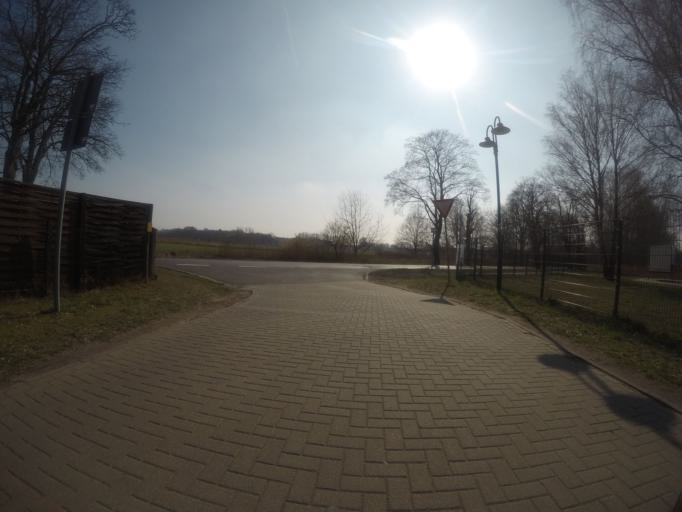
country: DE
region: Brandenburg
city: Bestensee
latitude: 52.2855
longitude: 13.7472
